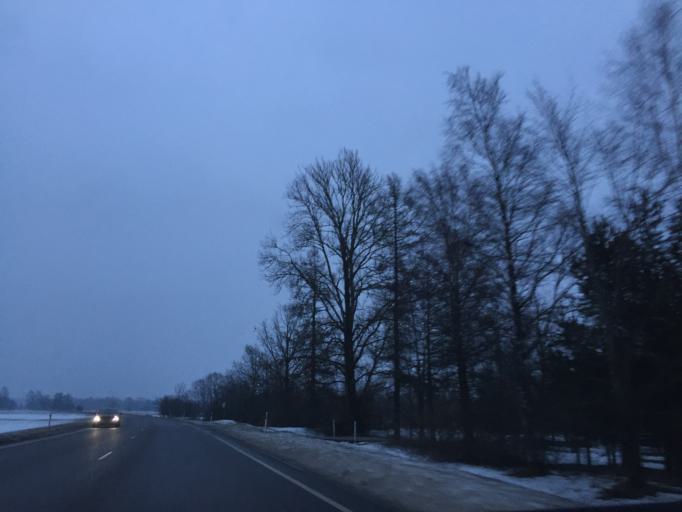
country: EE
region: Paernumaa
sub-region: Audru vald
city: Audru
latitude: 58.4253
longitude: 24.2936
